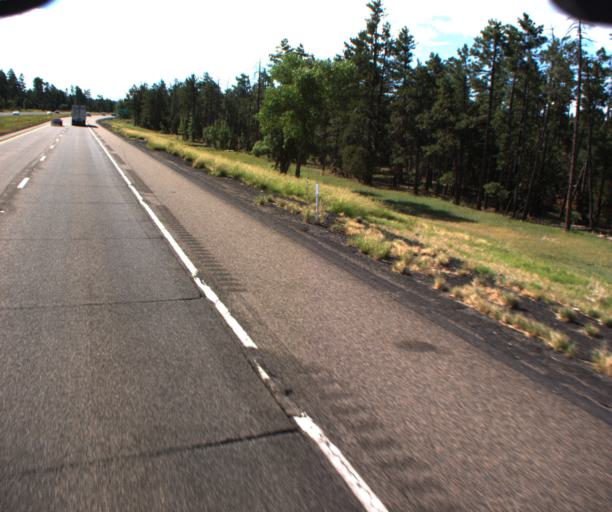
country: US
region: Arizona
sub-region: Coconino County
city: Sedona
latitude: 34.8590
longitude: -111.6129
